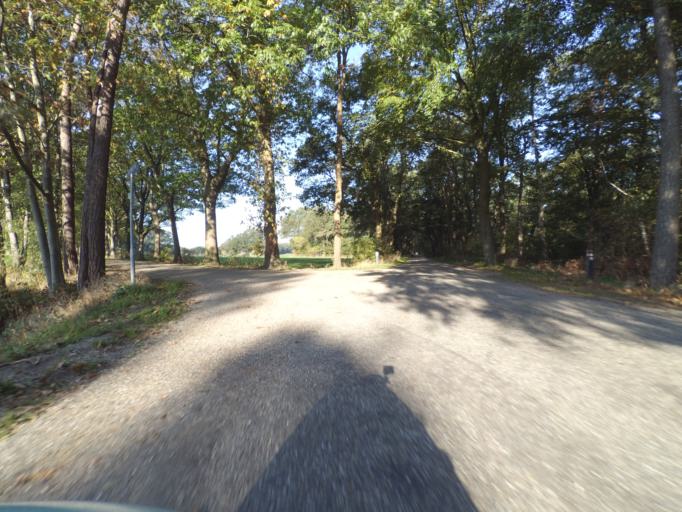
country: NL
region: Gelderland
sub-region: Berkelland
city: Eibergen
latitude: 52.0900
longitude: 6.6771
